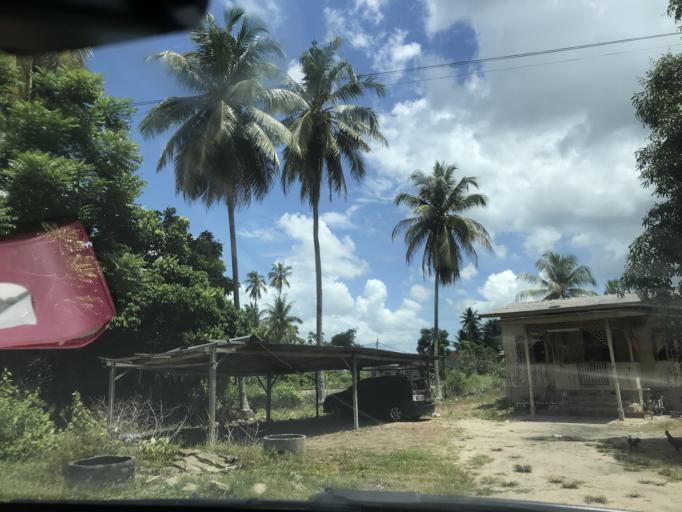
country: MY
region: Kelantan
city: Kota Bharu
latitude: 6.1633
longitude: 102.2078
